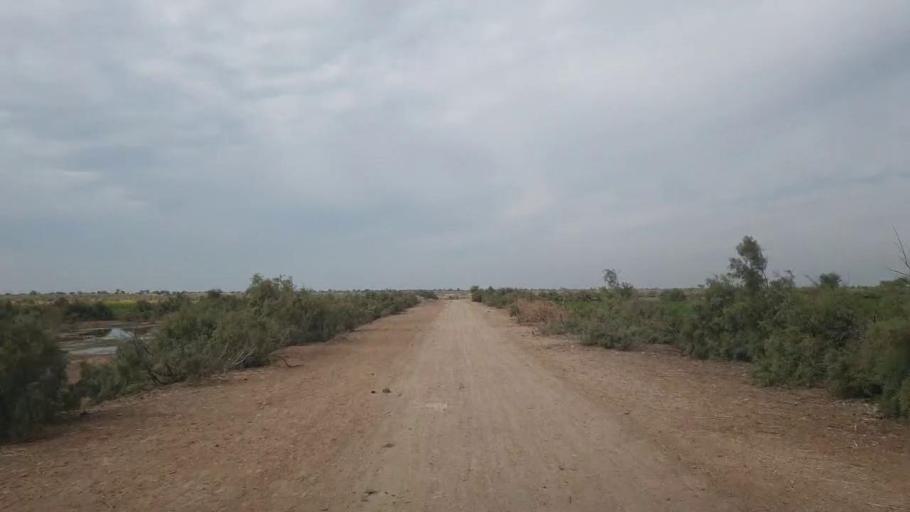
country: PK
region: Sindh
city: Sanghar
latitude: 26.0477
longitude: 68.9054
